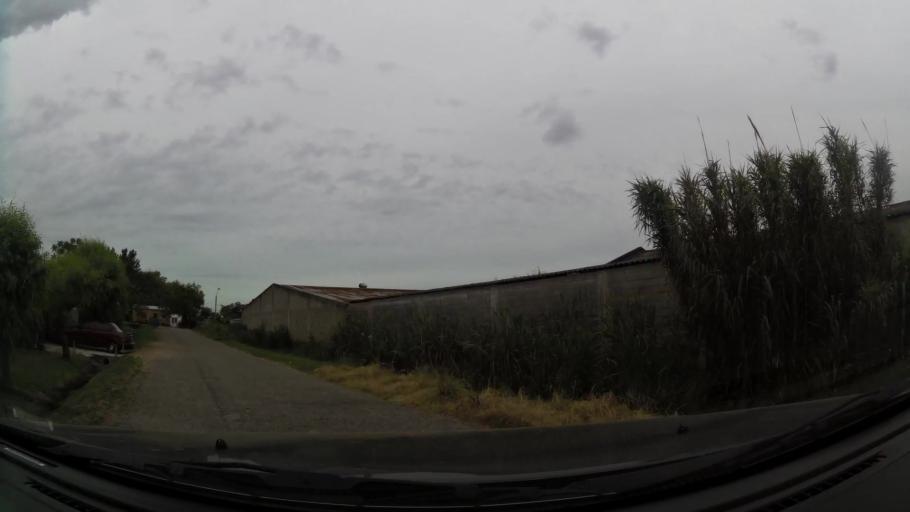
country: UY
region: Canelones
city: Las Piedras
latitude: -34.7101
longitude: -56.2059
